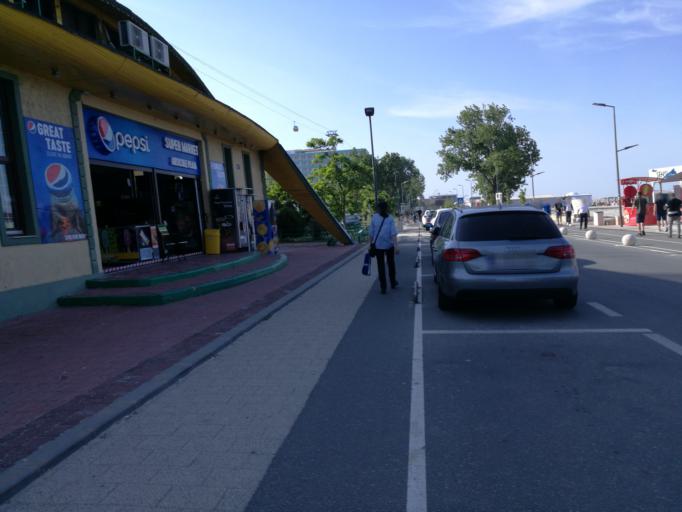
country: RO
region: Constanta
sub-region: Municipiul Constanta
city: Palazu Mare
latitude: 44.2289
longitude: 28.6286
